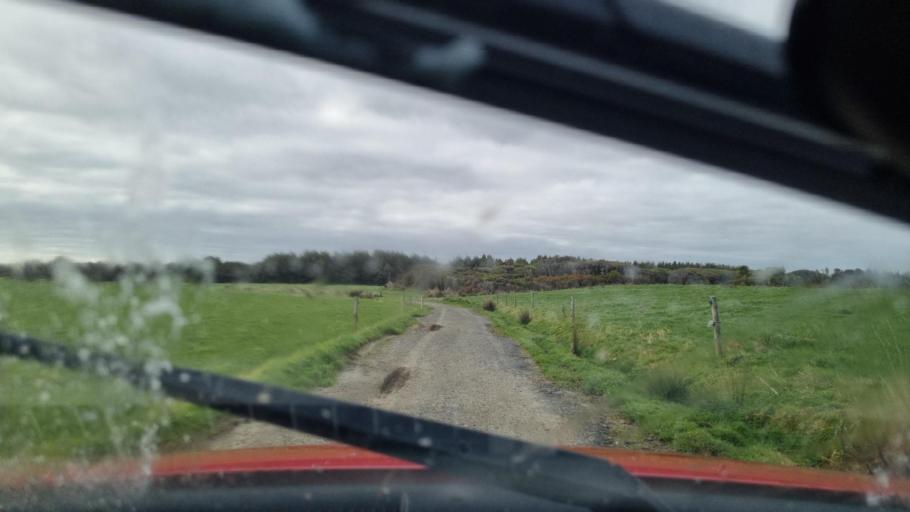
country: NZ
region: Southland
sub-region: Invercargill City
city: Bluff
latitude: -46.5171
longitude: 168.2946
